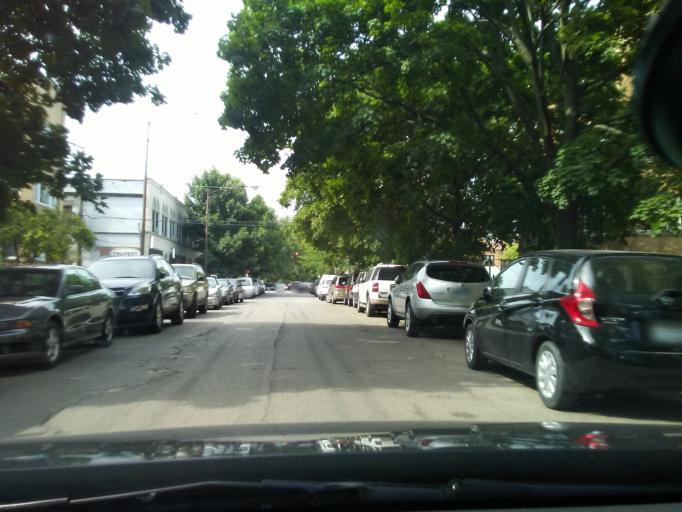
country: US
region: Illinois
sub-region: Cook County
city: Lincolnwood
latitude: 41.9675
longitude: -87.7182
